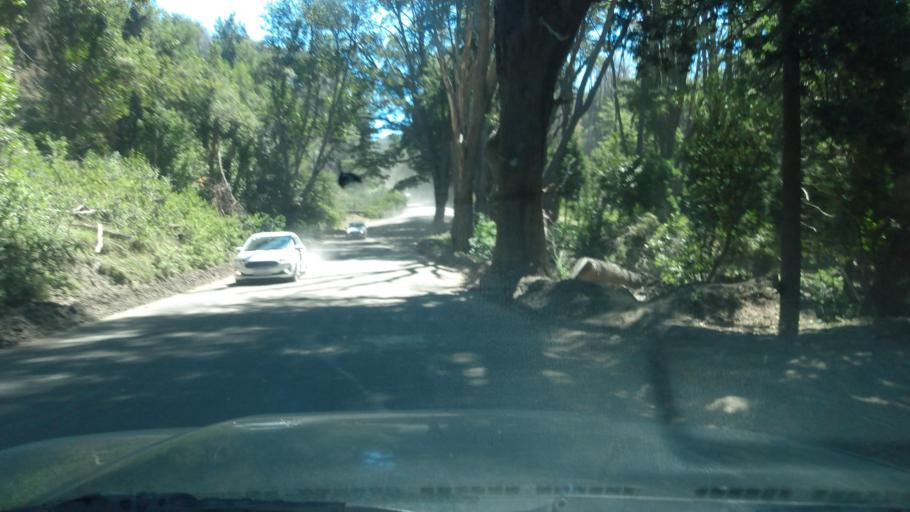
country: AR
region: Neuquen
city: Villa La Angostura
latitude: -40.6167
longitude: -71.5280
